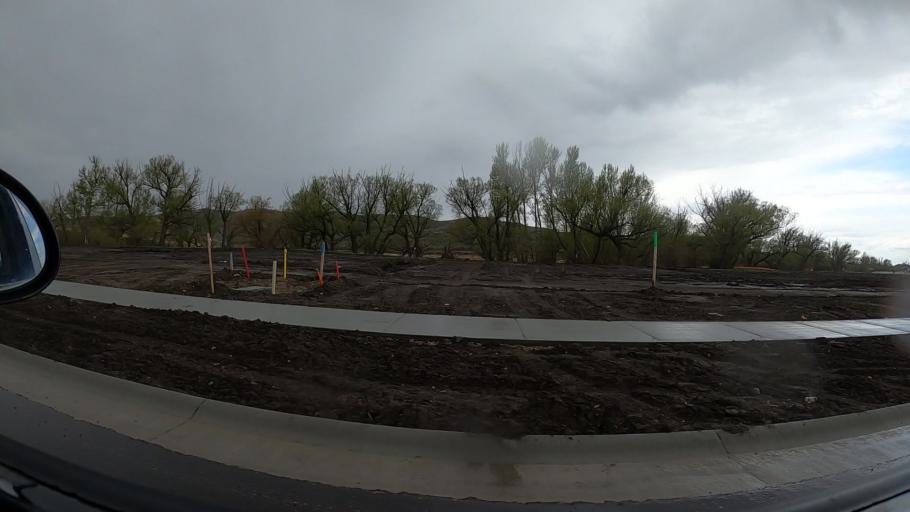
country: US
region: Idaho
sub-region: Ada County
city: Eagle
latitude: 43.7319
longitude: -116.2823
